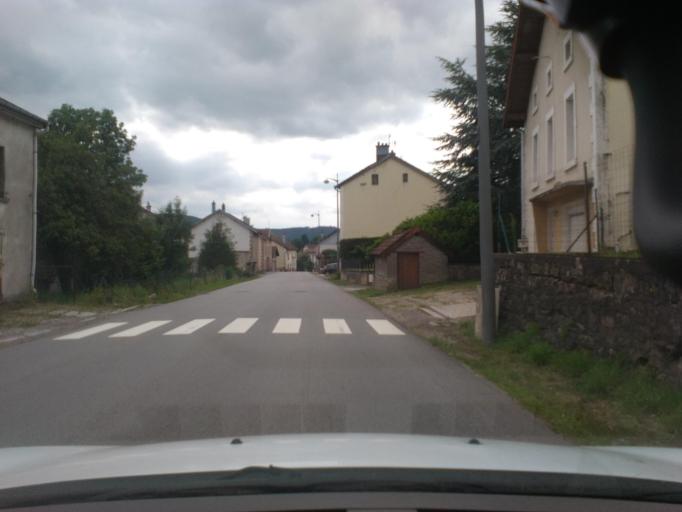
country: FR
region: Lorraine
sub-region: Departement des Vosges
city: Bruyeres
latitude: 48.1759
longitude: 6.6750
